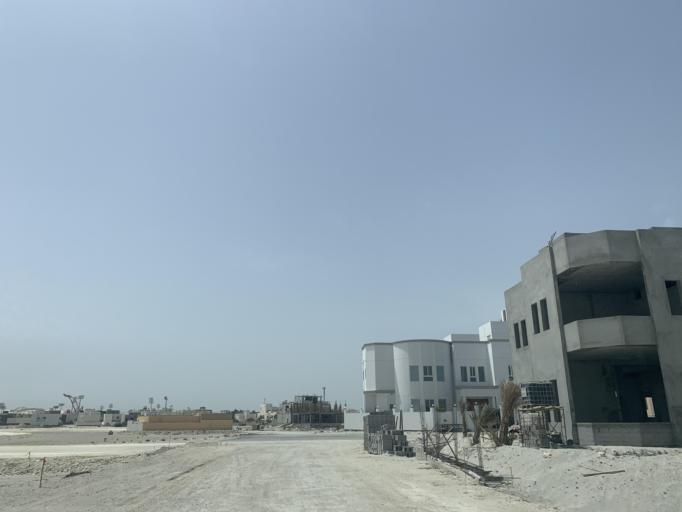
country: BH
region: Northern
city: Madinat `Isa
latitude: 26.1538
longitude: 50.5561
